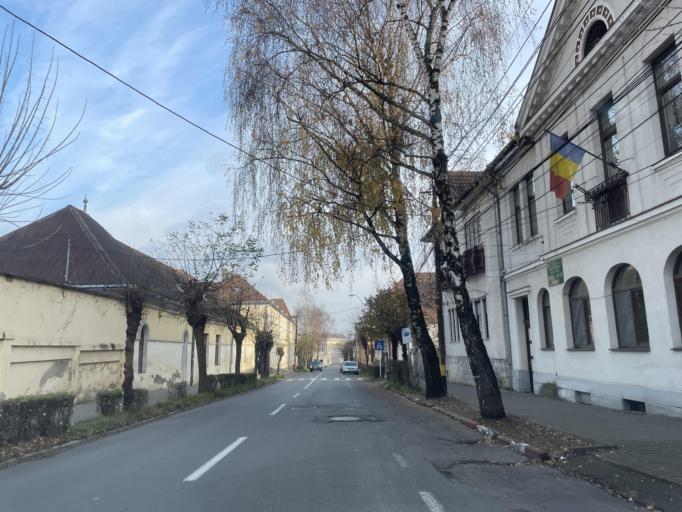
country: RO
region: Mures
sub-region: Municipiul Reghin
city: Reghin
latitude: 46.7814
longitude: 24.6980
